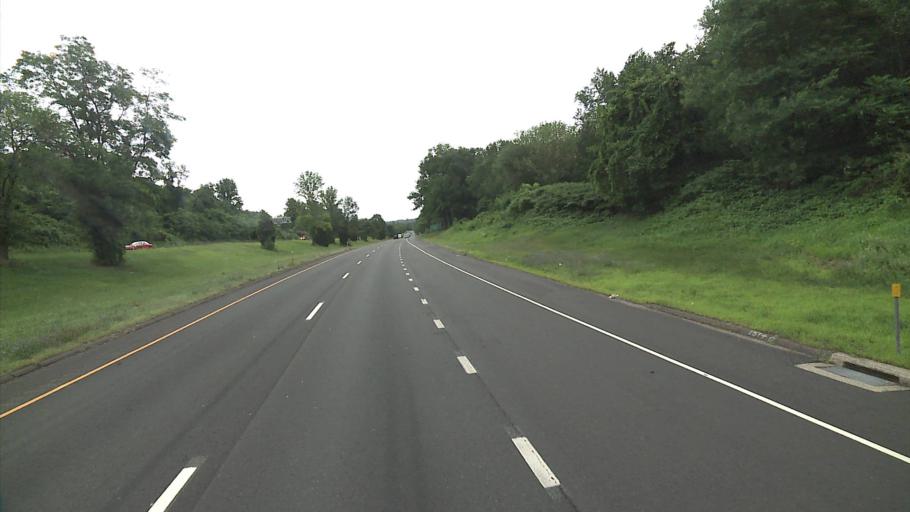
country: US
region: Connecticut
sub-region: Fairfield County
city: Trumbull
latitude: 41.2577
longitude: -73.1428
